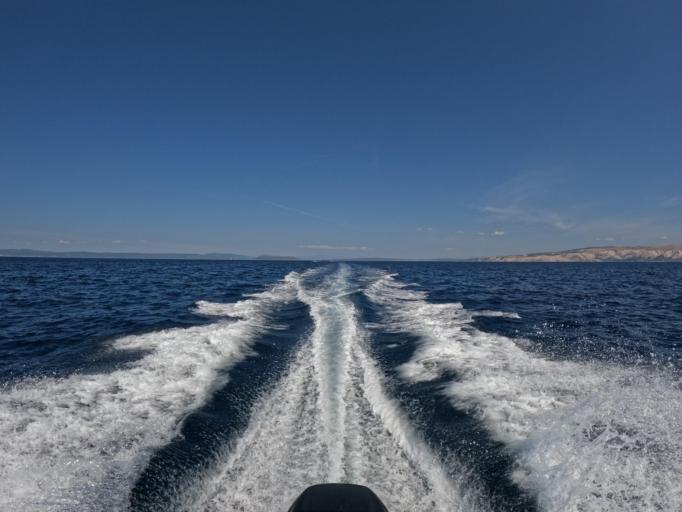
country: HR
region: Primorsko-Goranska
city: Lopar
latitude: 44.8893
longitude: 14.6461
